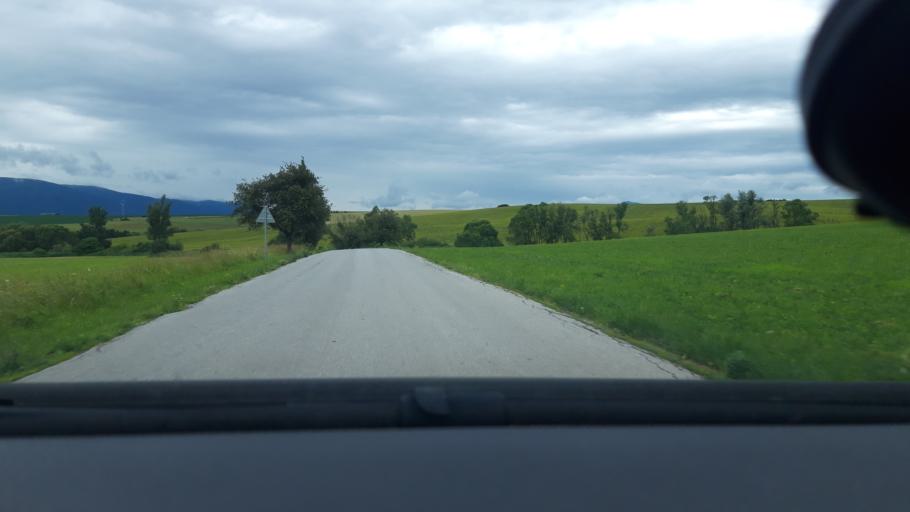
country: SK
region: Zilinsky
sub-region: Okres Martin
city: Martin
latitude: 48.9702
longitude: 18.9360
